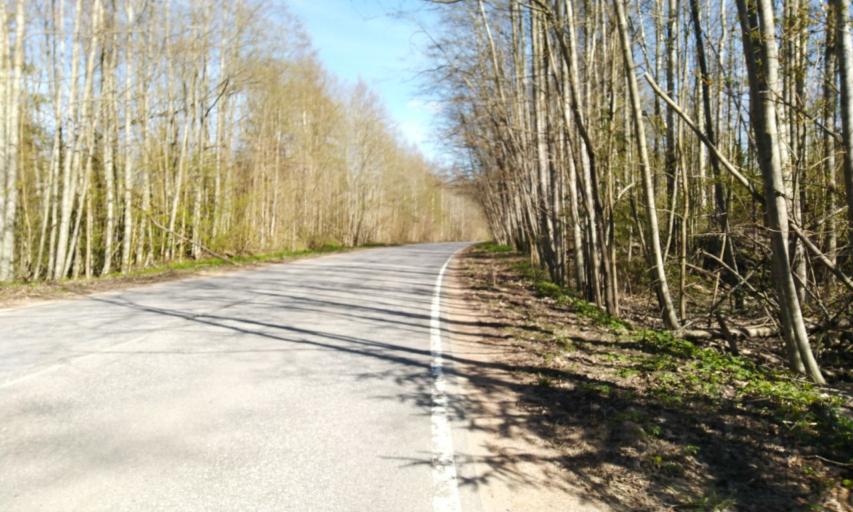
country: RU
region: Leningrad
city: Garbolovo
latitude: 60.4117
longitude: 30.4581
